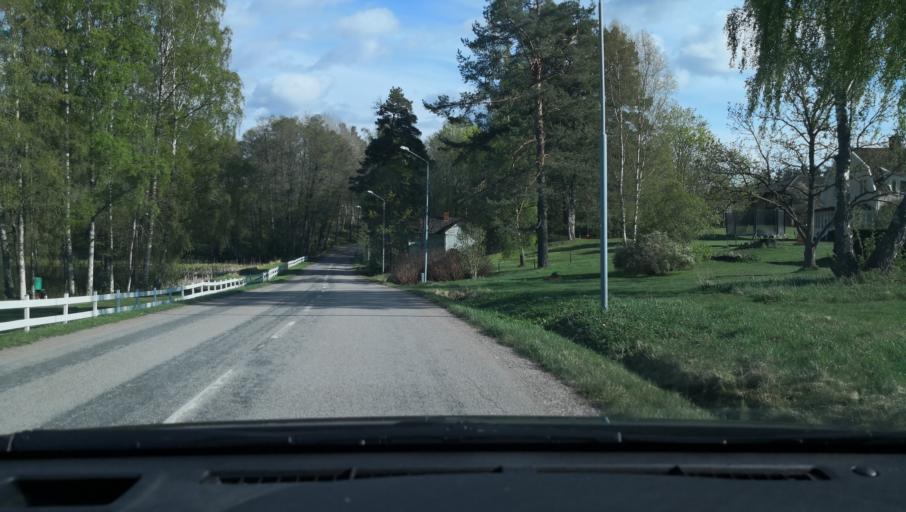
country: SE
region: OErebro
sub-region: Askersunds Kommun
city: Asbro
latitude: 58.9824
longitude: 15.0568
